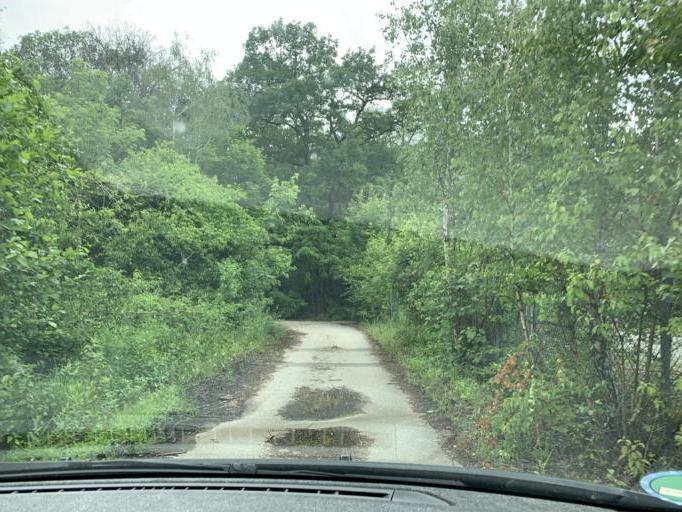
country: DE
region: North Rhine-Westphalia
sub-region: Regierungsbezirk Koln
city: Niederzier
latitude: 50.8795
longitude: 6.5063
